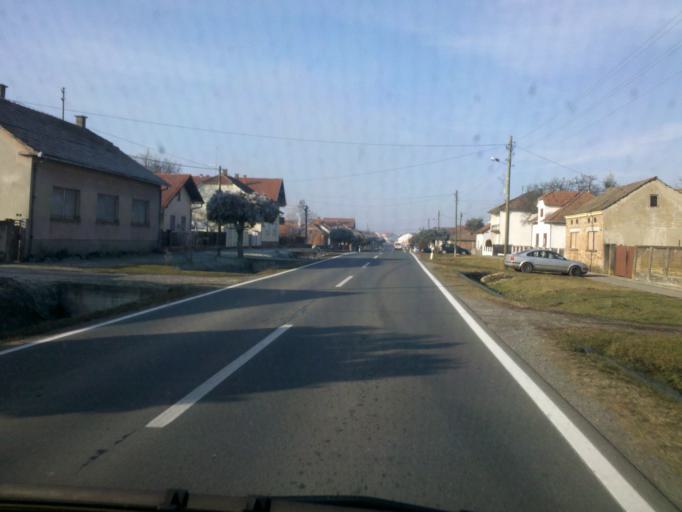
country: HR
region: Koprivnicko-Krizevacka
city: Kalinovac
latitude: 45.9803
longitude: 17.1630
